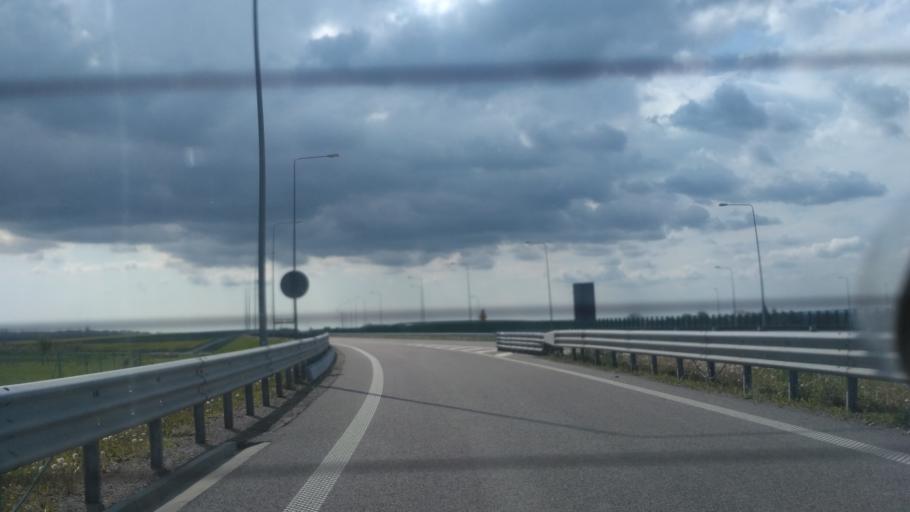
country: PL
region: Subcarpathian Voivodeship
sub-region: Powiat jaroslawski
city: Pawlosiow
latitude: 49.9717
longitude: 22.6466
